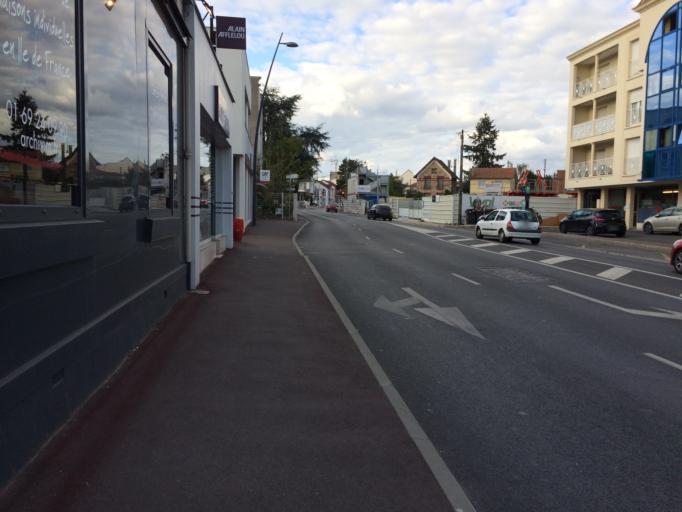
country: FR
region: Ile-de-France
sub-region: Departement de l'Essonne
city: Savigny-sur-Orge
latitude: 48.6810
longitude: 2.3427
